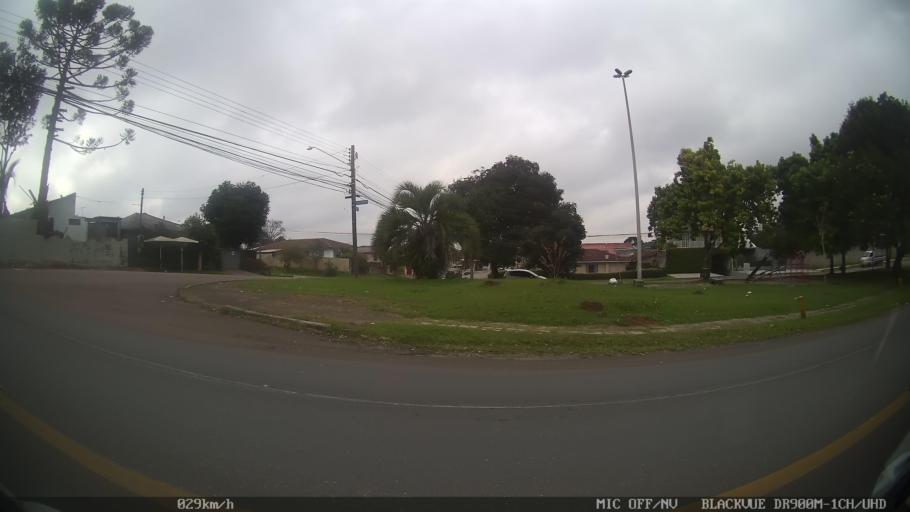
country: BR
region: Parana
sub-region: Almirante Tamandare
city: Almirante Tamandare
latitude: -25.3665
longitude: -49.2727
